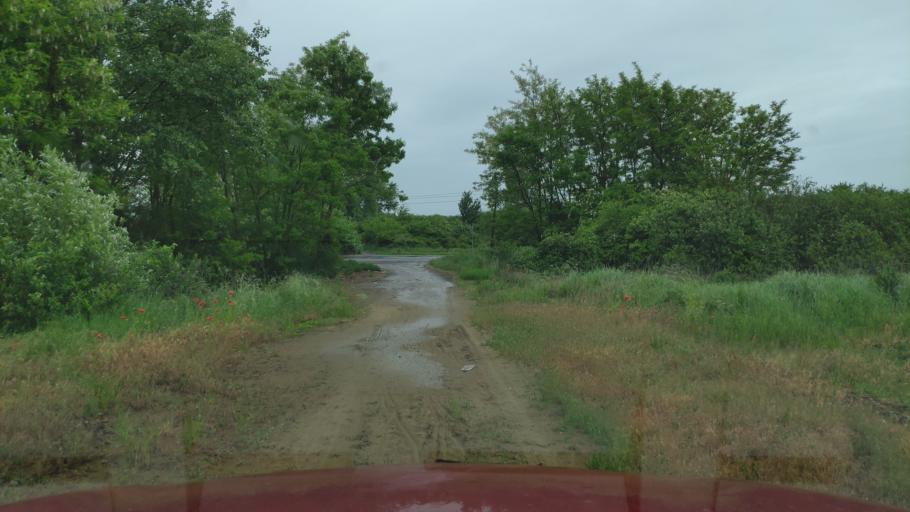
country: SK
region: Kosicky
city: Cierna nad Tisou
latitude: 48.4286
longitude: 22.0210
